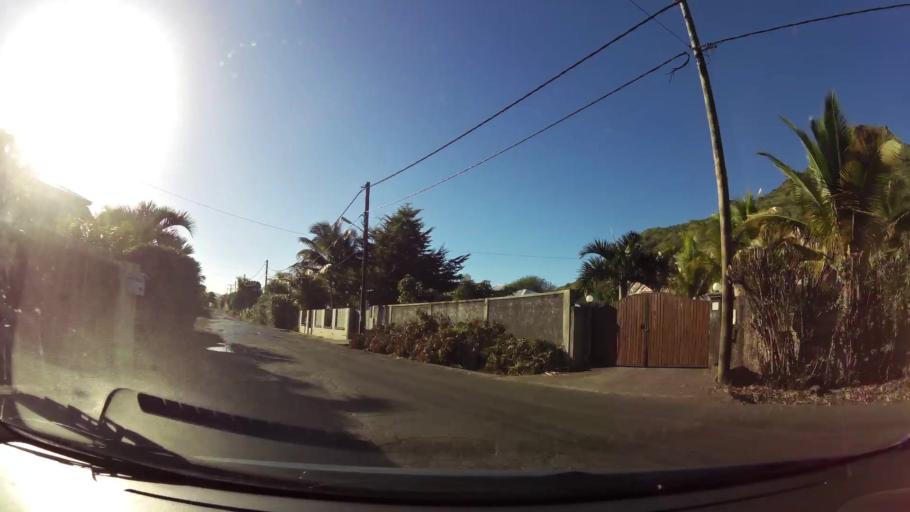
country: MU
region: Black River
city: Tamarin
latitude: -20.3368
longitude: 57.3725
